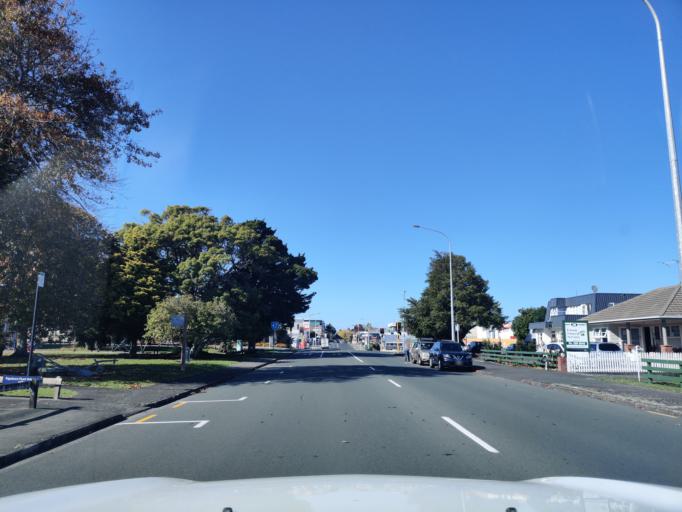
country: NZ
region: Auckland
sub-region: Auckland
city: Papakura
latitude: -37.0611
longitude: 174.9395
